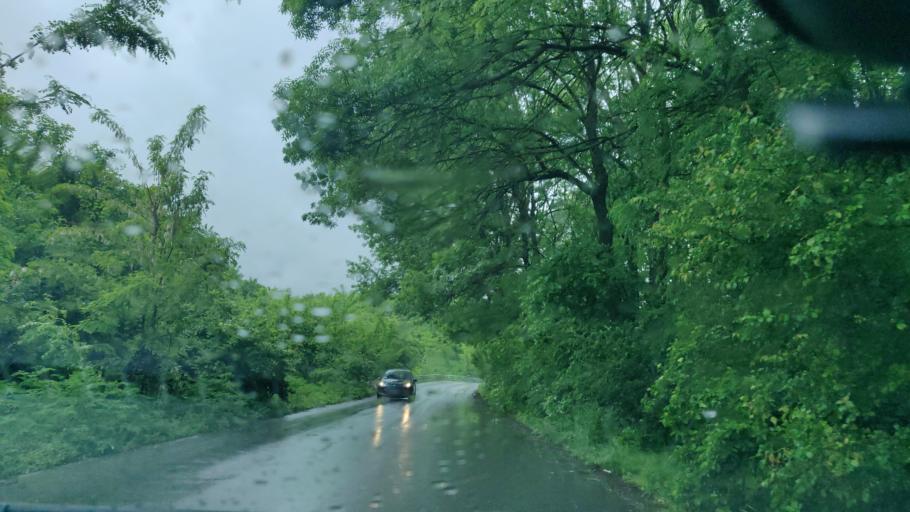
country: RO
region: Giurgiu
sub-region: Comuna Bulbucata
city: Bulbucata
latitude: 44.2891
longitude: 25.7767
